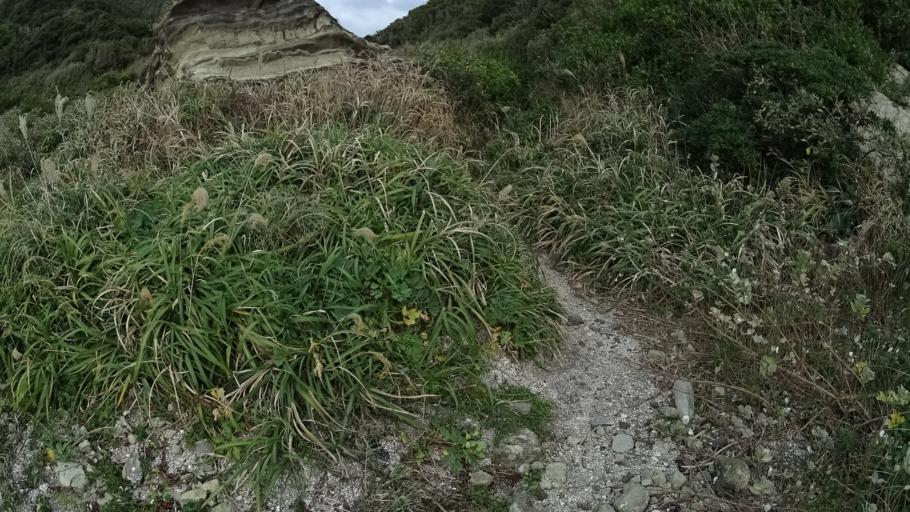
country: JP
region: Kanagawa
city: Miura
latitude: 35.1394
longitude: 139.6405
